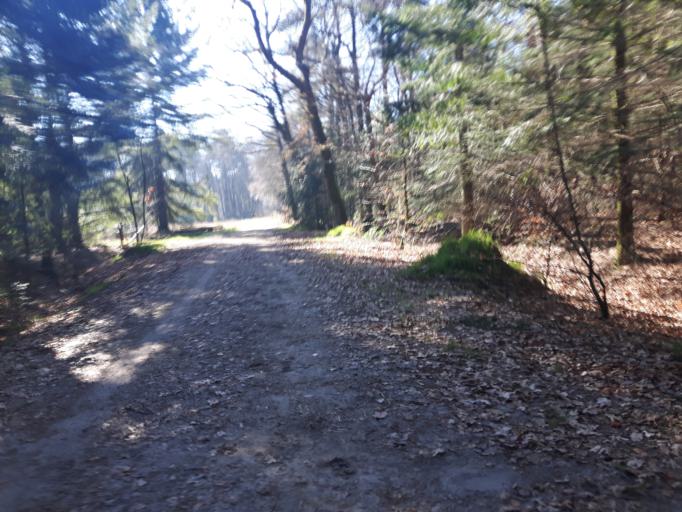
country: NL
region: Overijssel
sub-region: Gemeente Haaksbergen
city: Haaksbergen
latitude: 52.1660
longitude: 6.8179
